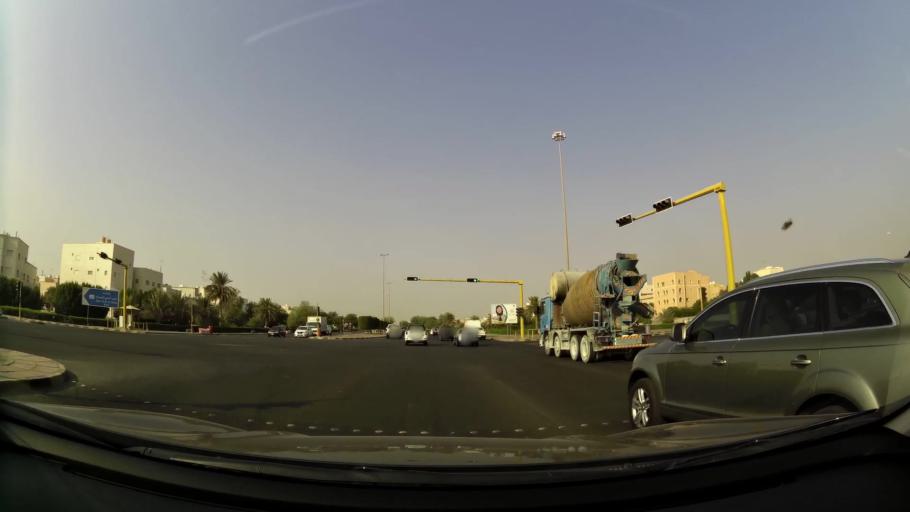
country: KW
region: Mubarak al Kabir
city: Mubarak al Kabir
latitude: 29.1805
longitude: 48.0829
